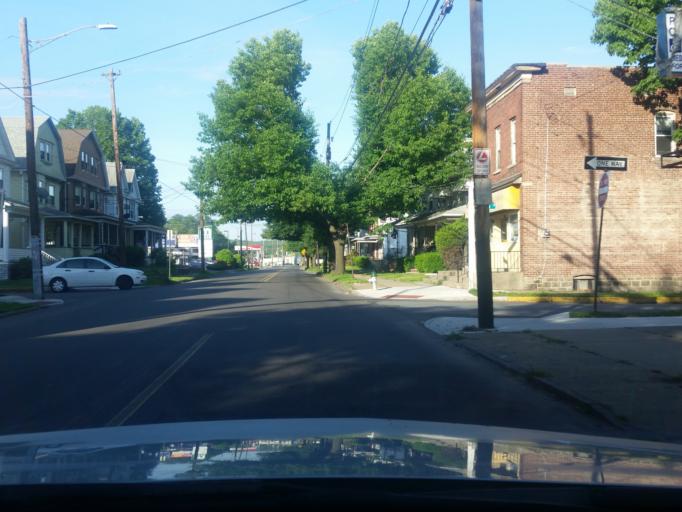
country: US
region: Pennsylvania
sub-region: Luzerne County
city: Larksville
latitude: 41.2365
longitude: -75.9154
